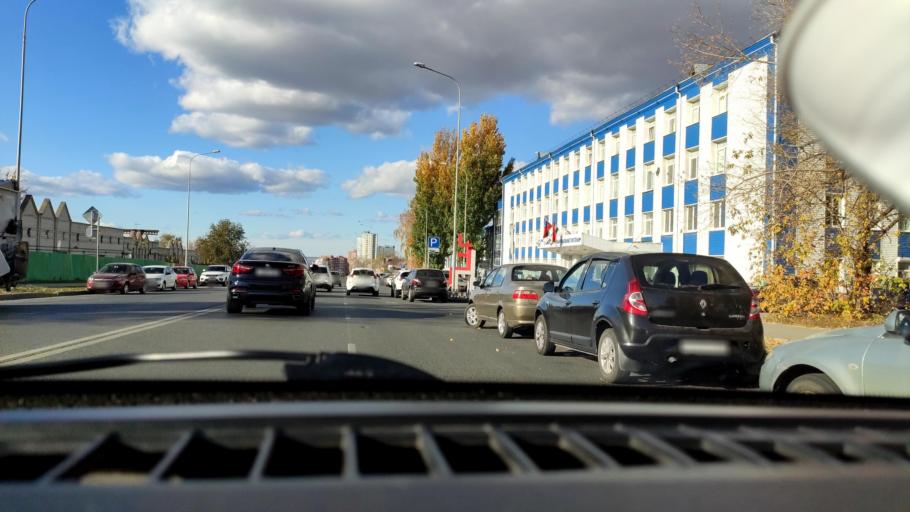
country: RU
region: Samara
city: Samara
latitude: 53.2049
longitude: 50.1579
